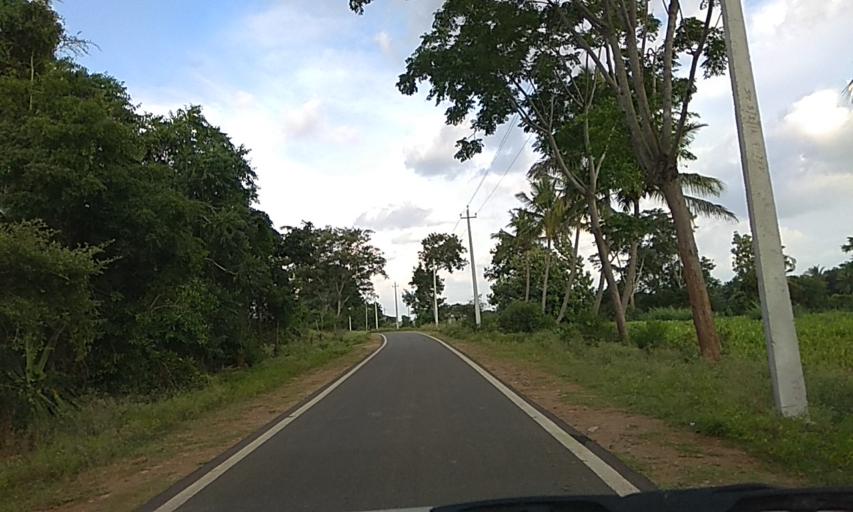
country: IN
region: Karnataka
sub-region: Chamrajnagar
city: Gundlupet
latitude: 11.7621
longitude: 76.7739
